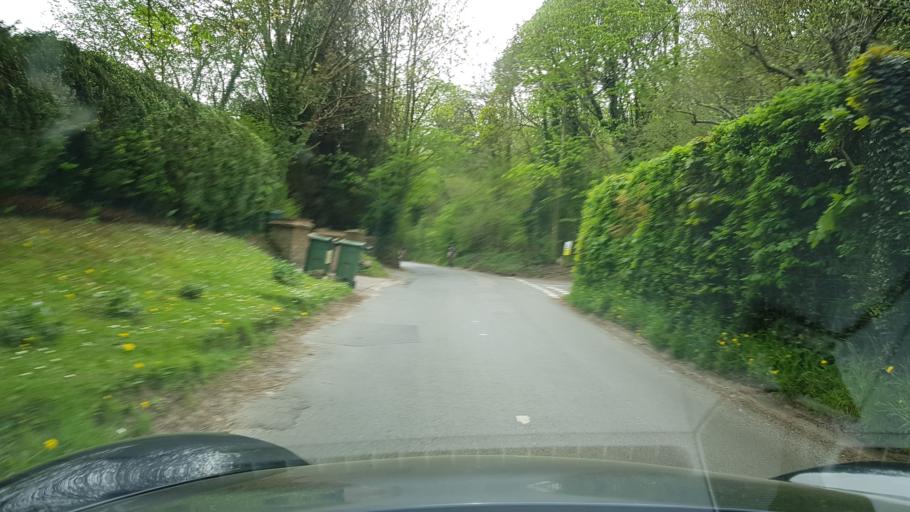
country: GB
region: England
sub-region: Surrey
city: East Horsley
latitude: 51.2504
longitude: -0.4315
